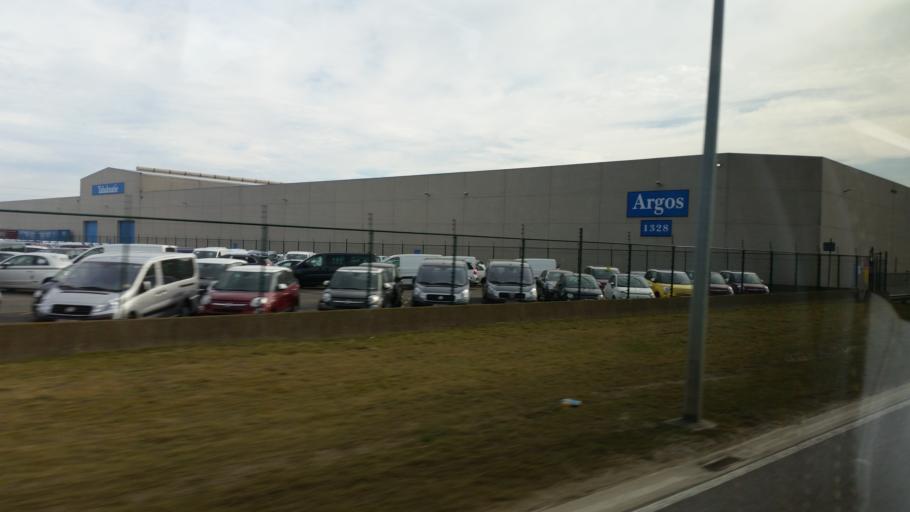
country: BE
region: Flanders
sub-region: Provincie Oost-Vlaanderen
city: Beveren
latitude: 51.2695
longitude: 4.2006
